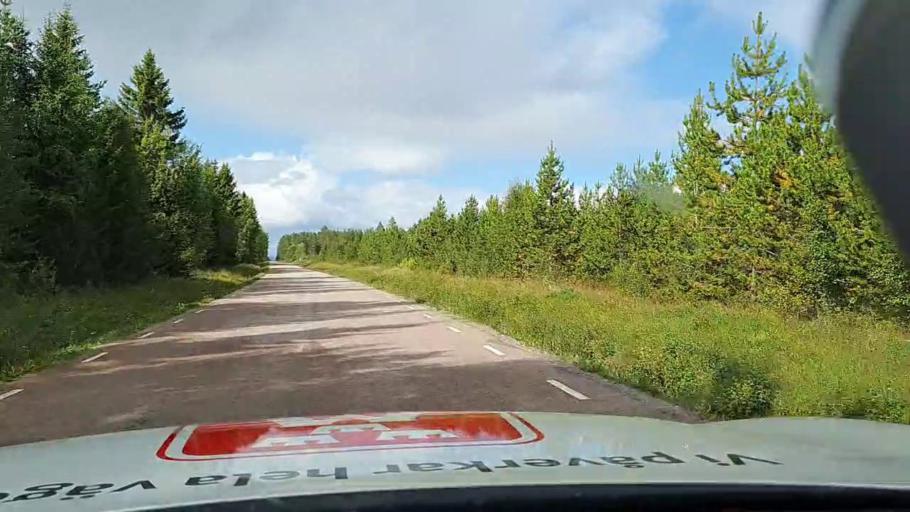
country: SE
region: Jaemtland
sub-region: Stroemsunds Kommun
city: Stroemsund
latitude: 63.8637
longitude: 15.3830
